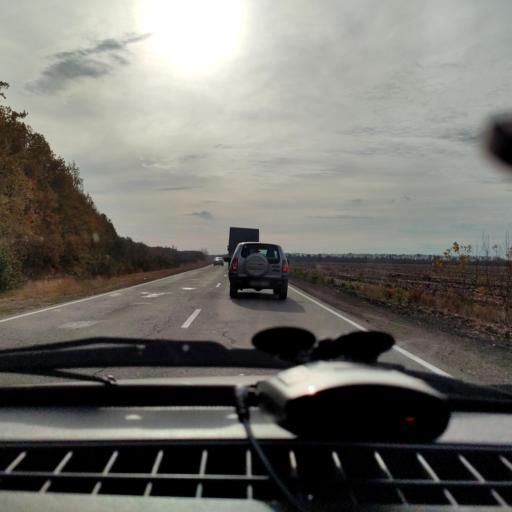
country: RU
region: Voronezj
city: Shilovo
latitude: 51.4413
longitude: 38.9966
